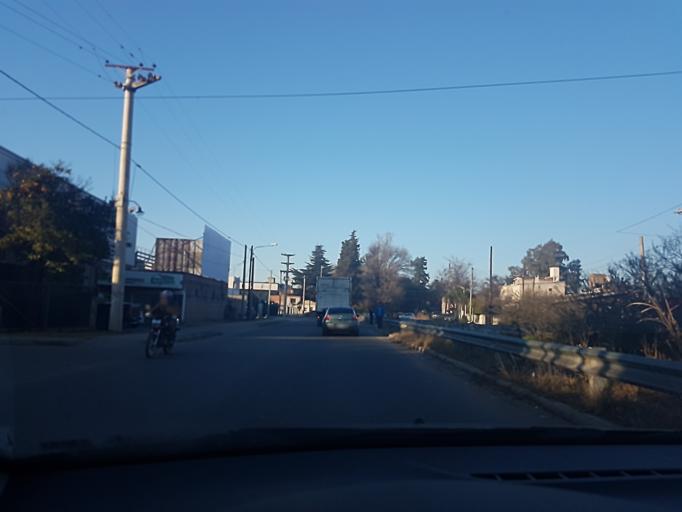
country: AR
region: Cordoba
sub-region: Departamento de Capital
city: Cordoba
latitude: -31.3422
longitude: -64.2256
